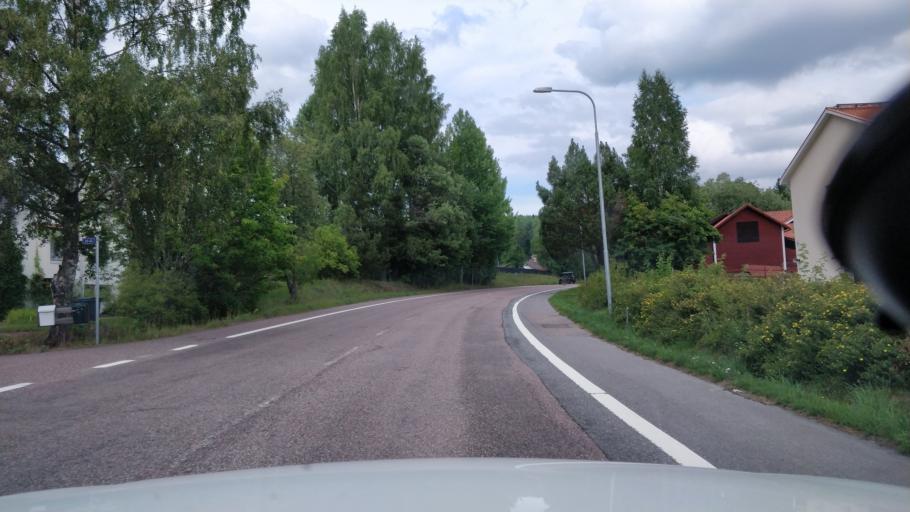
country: SE
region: Dalarna
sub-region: Faluns Kommun
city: Bjursas
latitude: 60.7375
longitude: 15.4401
